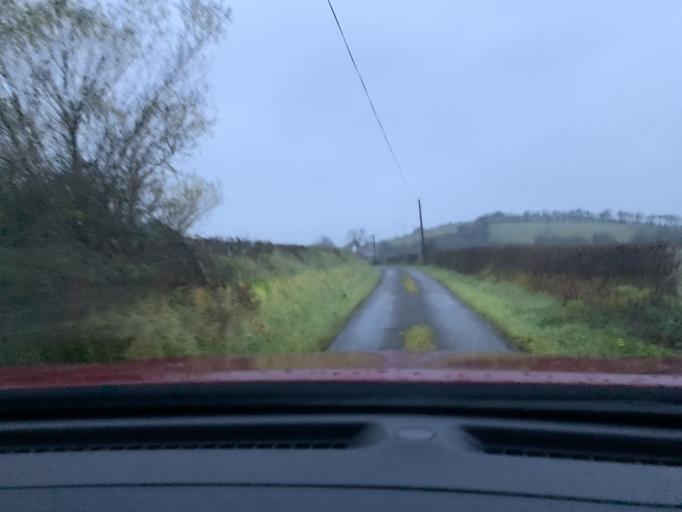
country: IE
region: Connaught
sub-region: Sligo
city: Ballymote
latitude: 54.0192
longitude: -8.5359
